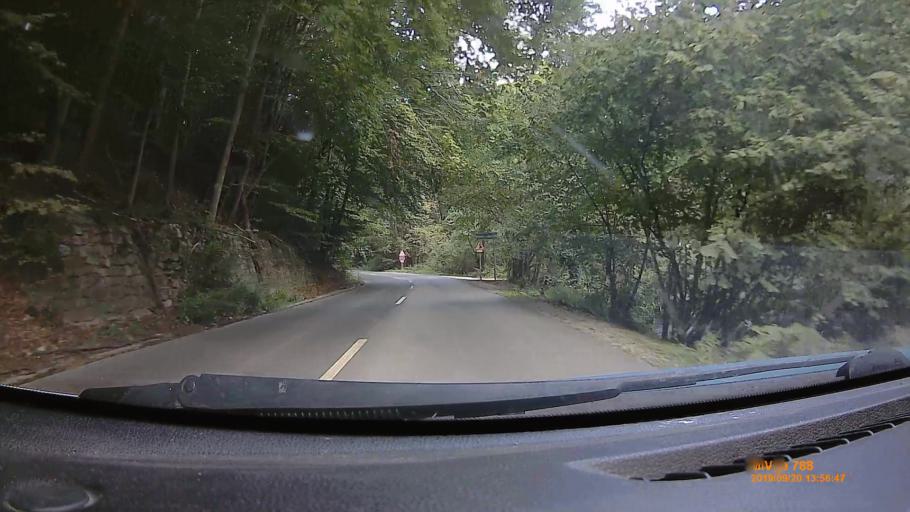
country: HU
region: Borsod-Abauj-Zemplen
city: Sajobabony
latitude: 48.0885
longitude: 20.6190
